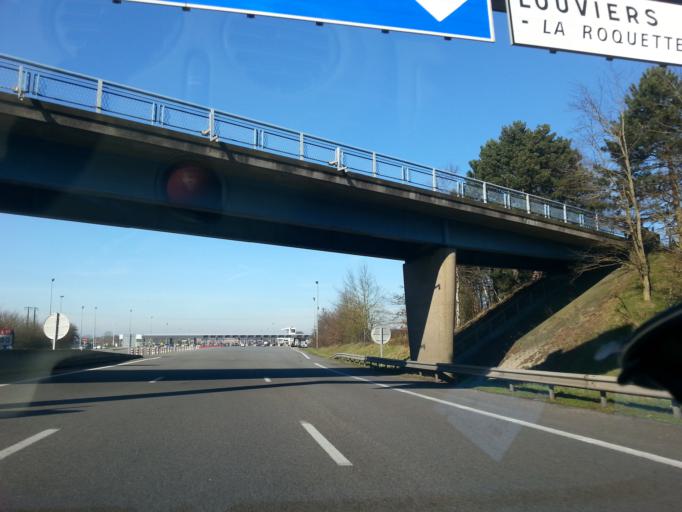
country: FR
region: Haute-Normandie
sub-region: Departement de l'Eure
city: Ande
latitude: 49.1885
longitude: 1.2346
